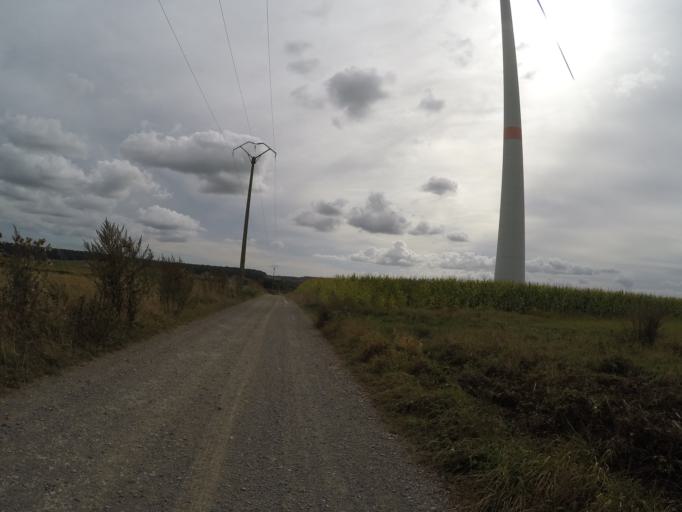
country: BE
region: Wallonia
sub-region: Province de Namur
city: Dinant
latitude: 50.2949
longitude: 4.9842
